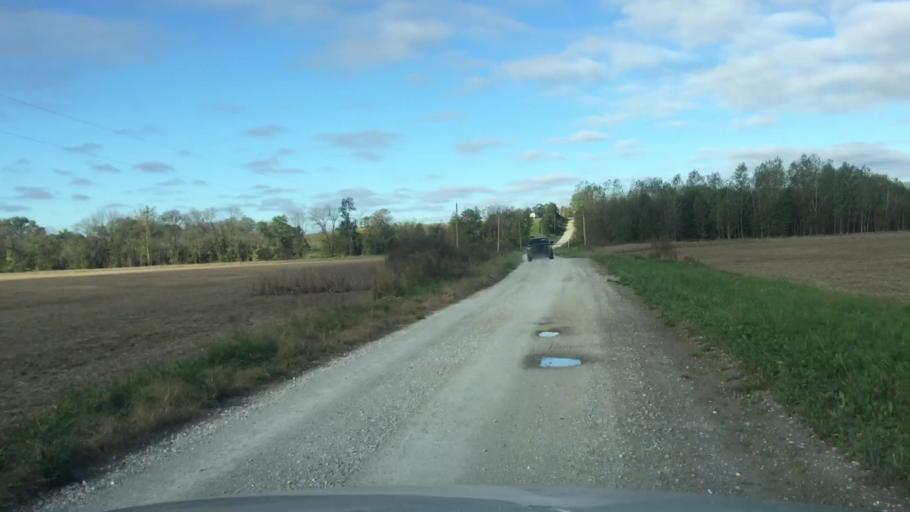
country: US
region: Missouri
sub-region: Howard County
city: New Franklin
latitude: 39.0833
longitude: -92.7673
